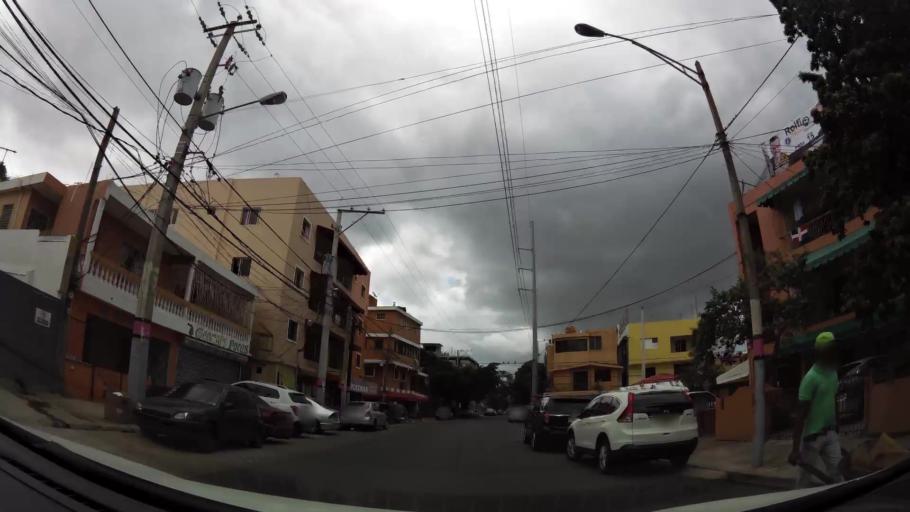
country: DO
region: Nacional
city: La Julia
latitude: 18.4539
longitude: -69.9317
